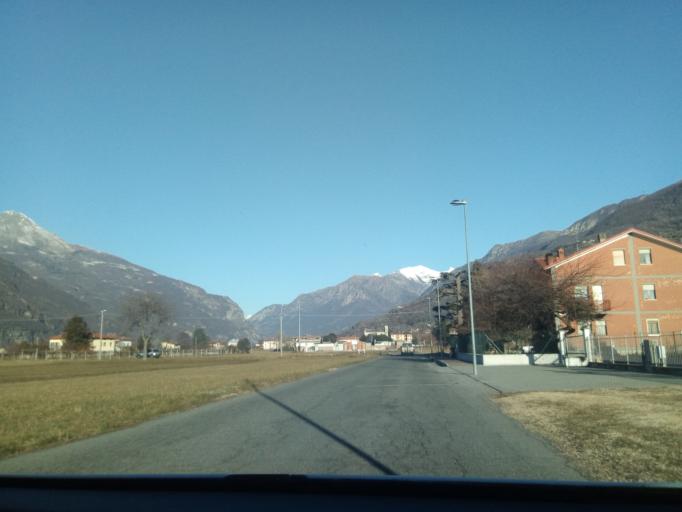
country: IT
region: Piedmont
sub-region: Provincia di Torino
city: Borgofranco d'Ivrea
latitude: 45.5206
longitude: 7.8553
